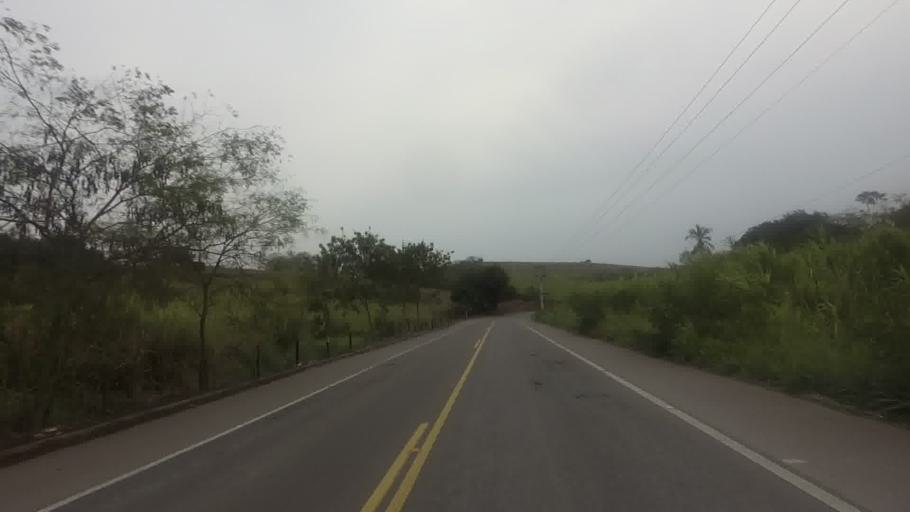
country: BR
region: Rio de Janeiro
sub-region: Santo Antonio De Padua
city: Santo Antonio de Padua
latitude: -21.5762
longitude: -42.2118
